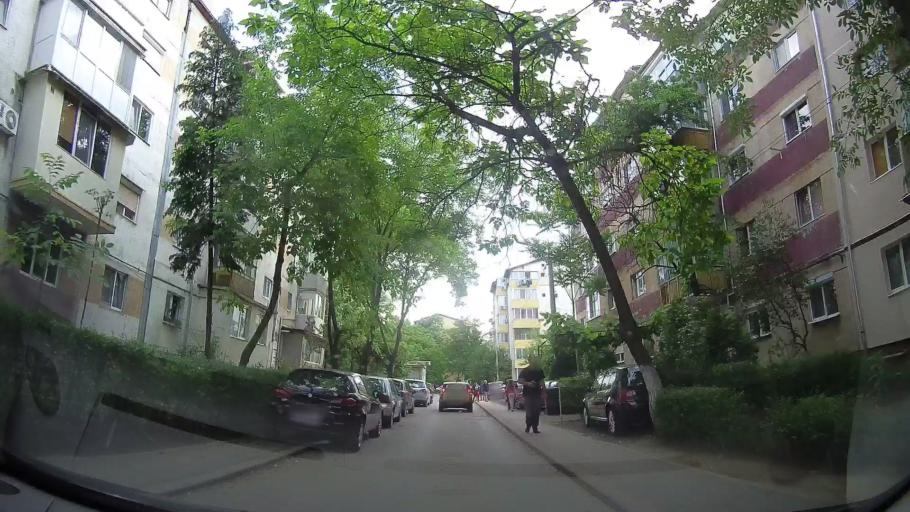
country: RO
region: Timis
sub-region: Comuna Dumbravita
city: Dumbravita
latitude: 45.7787
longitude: 21.2354
